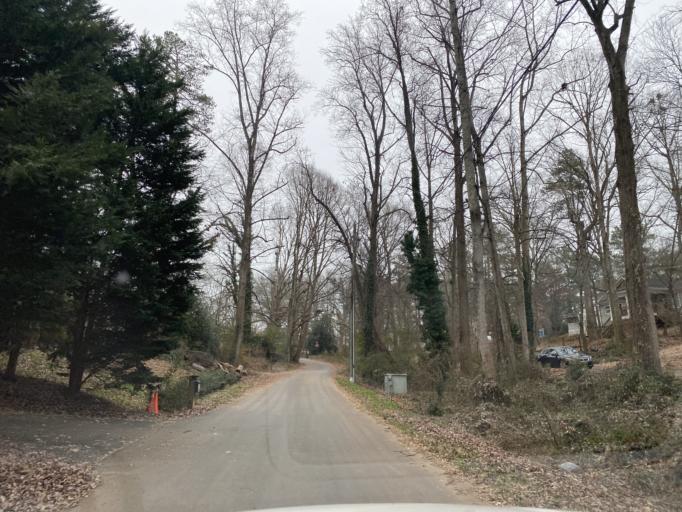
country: US
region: Georgia
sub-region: Cobb County
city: Fair Oaks
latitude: 33.9011
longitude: -84.5743
